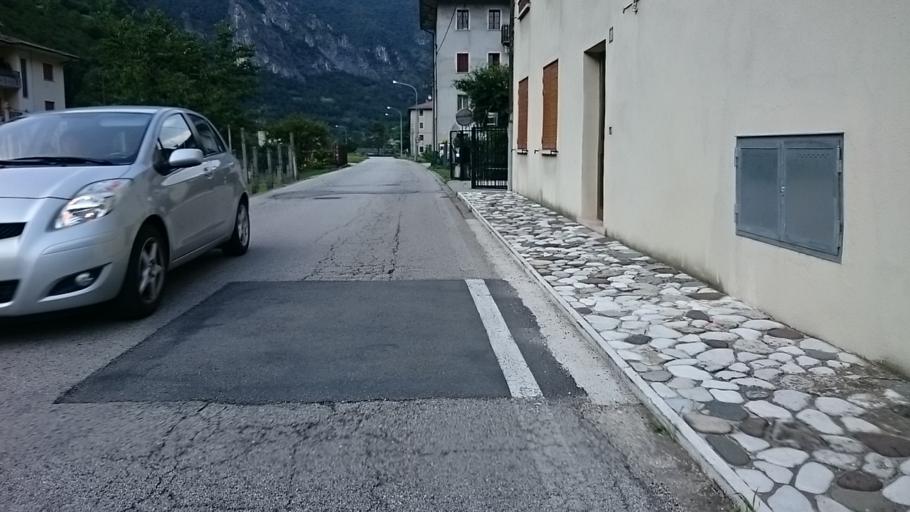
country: IT
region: Veneto
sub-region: Provincia di Vicenza
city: Valstagna
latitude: 45.8914
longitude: 11.6885
